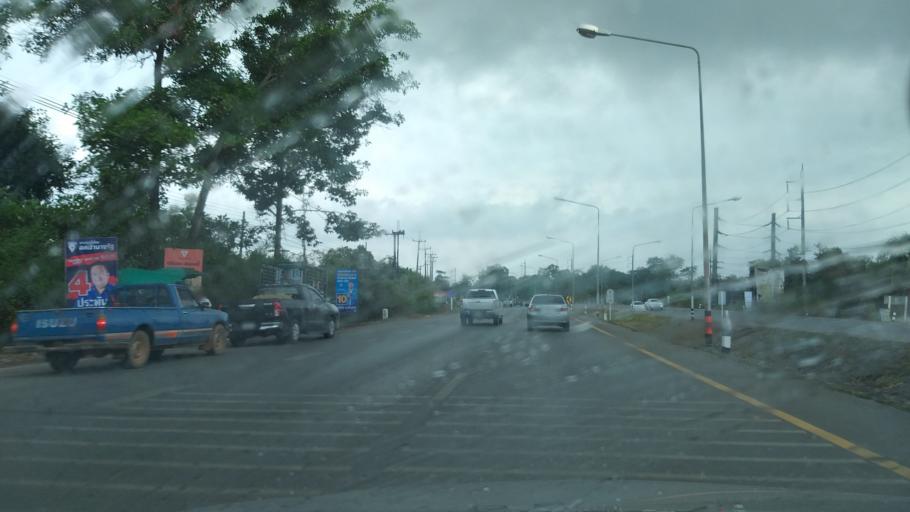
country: TH
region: Chanthaburi
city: Khlung
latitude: 12.4569
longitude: 102.2643
